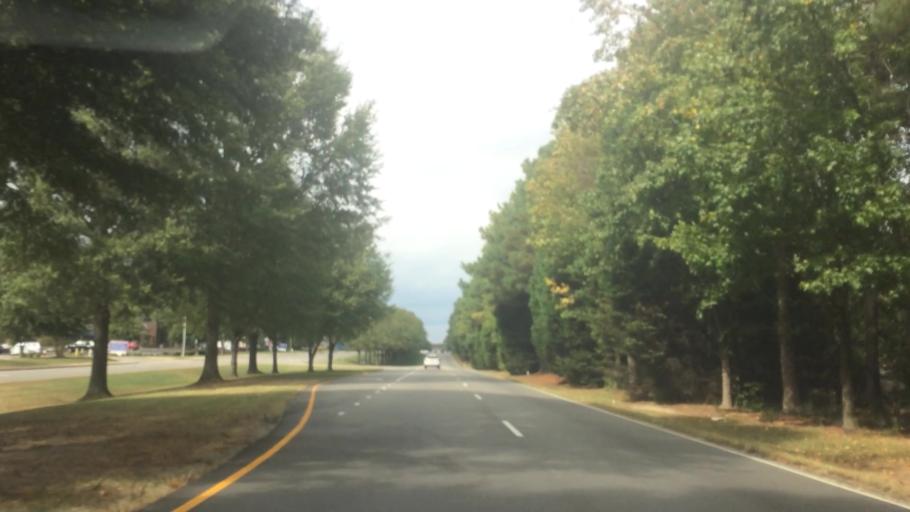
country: US
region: Virginia
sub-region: James City County
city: Williamsburg
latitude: 37.3074
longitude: -76.7298
